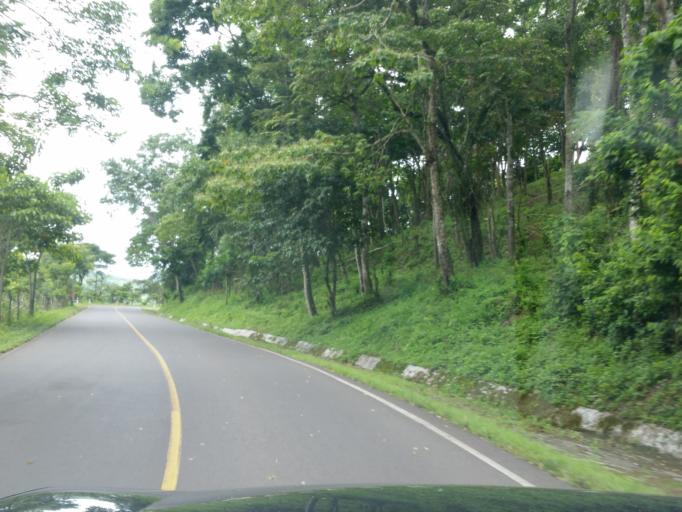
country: NI
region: Matagalpa
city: San Ramon
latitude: 13.0059
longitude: -85.8018
